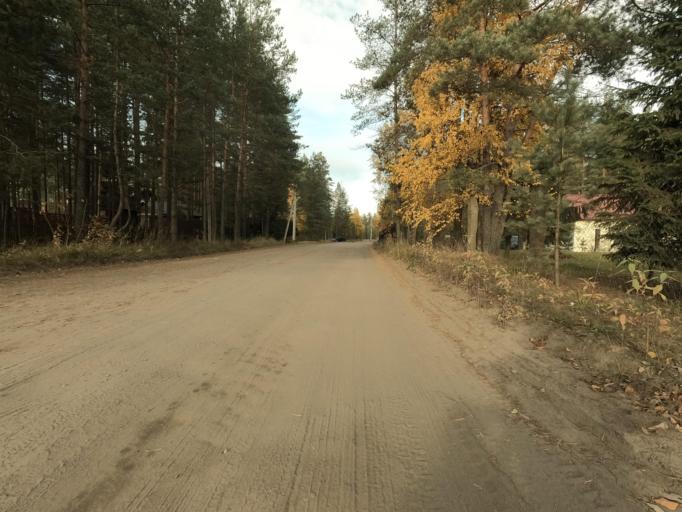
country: RU
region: Leningrad
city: Priladozhskiy
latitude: 59.6332
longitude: 31.3887
